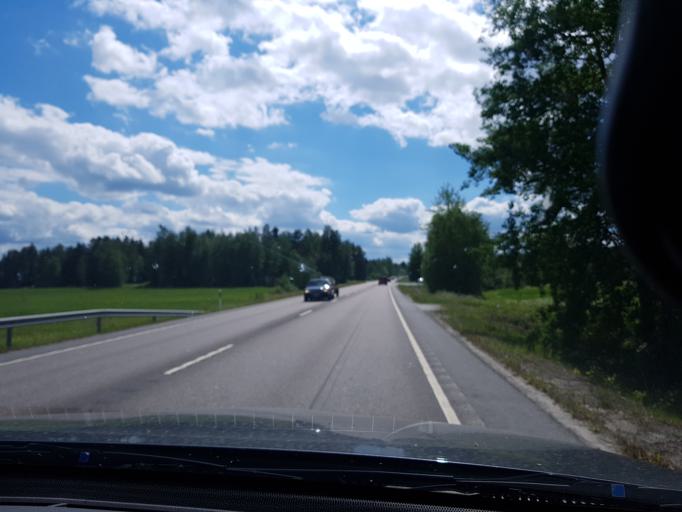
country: FI
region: Haeme
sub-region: Haemeenlinna
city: Parola
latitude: 61.1123
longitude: 24.4146
